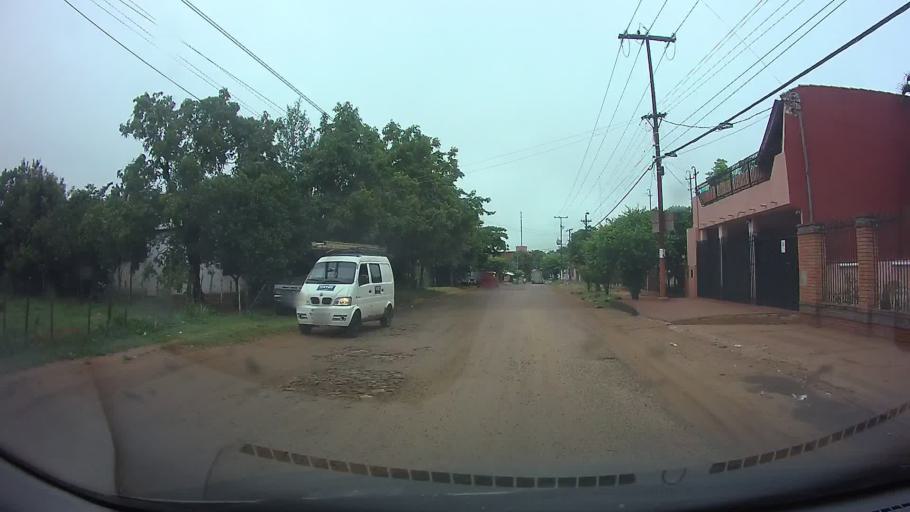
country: PY
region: Central
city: Itaugua
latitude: -25.3893
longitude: -57.3517
